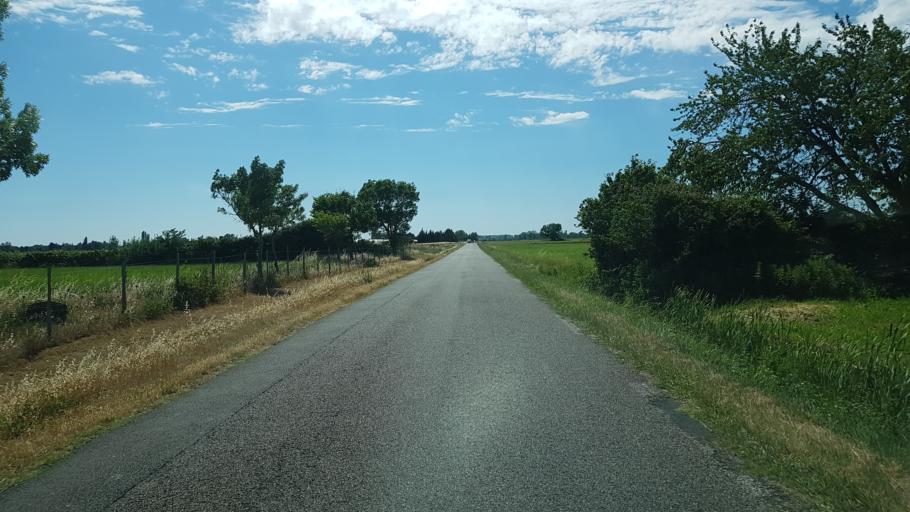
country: FR
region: Provence-Alpes-Cote d'Azur
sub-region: Departement des Bouches-du-Rhone
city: Saint-Martin-de-Crau
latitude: 43.6551
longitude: 4.7776
